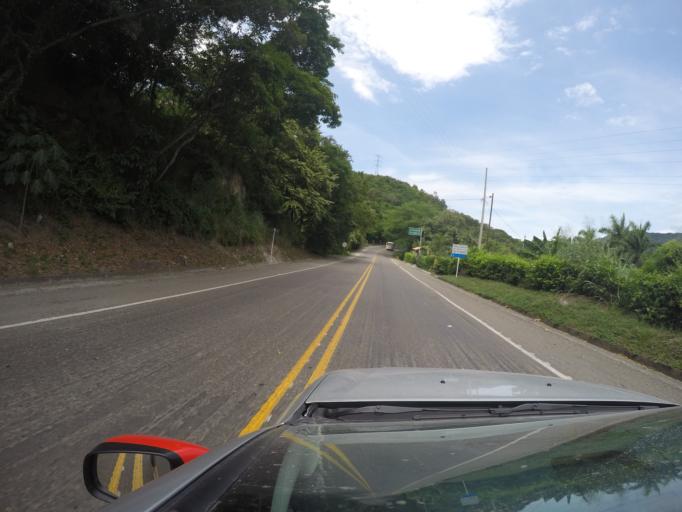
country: CO
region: Tolima
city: Honda
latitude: 5.2362
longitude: -74.7297
